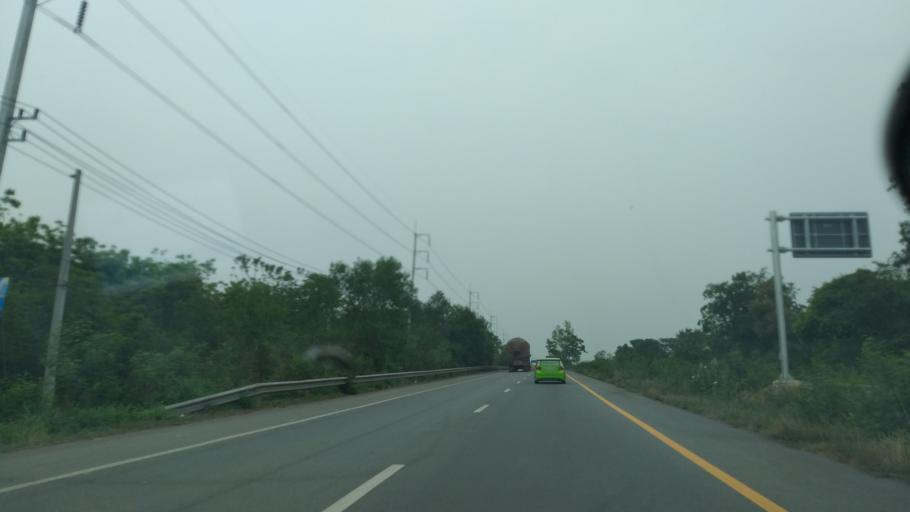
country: TH
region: Chon Buri
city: Ko Chan
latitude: 13.4499
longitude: 101.2835
